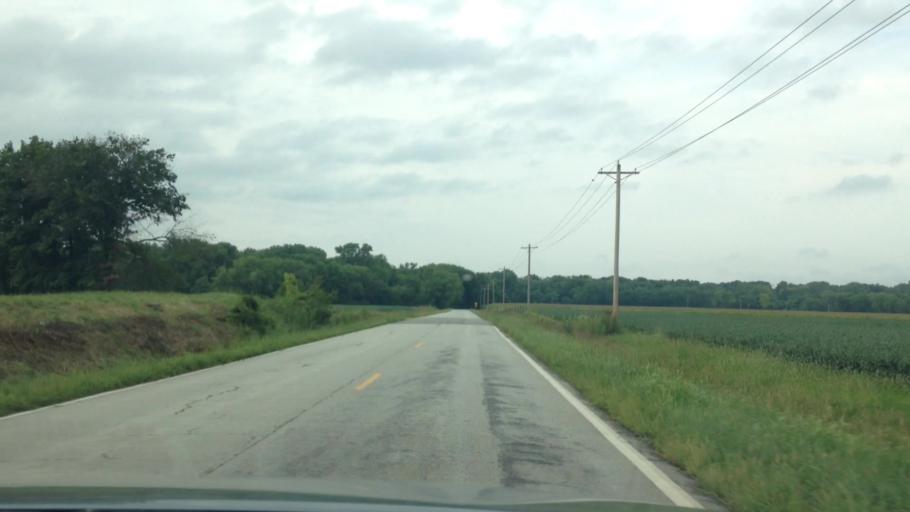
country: US
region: Missouri
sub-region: Clay County
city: Smithville
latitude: 39.3987
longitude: -94.6620
